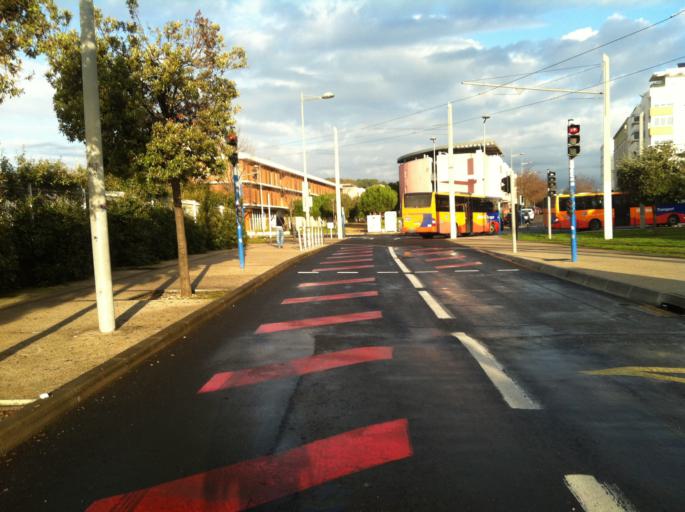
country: FR
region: Languedoc-Roussillon
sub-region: Departement de l'Herault
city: Montferrier-sur-Lez
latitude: 43.6355
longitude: 3.8476
